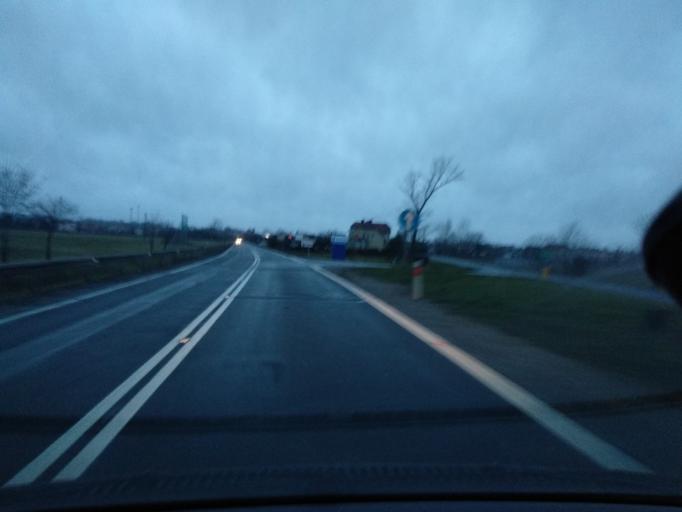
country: PL
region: Lower Silesian Voivodeship
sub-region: Powiat legnicki
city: Prochowice
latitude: 51.2689
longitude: 16.3739
